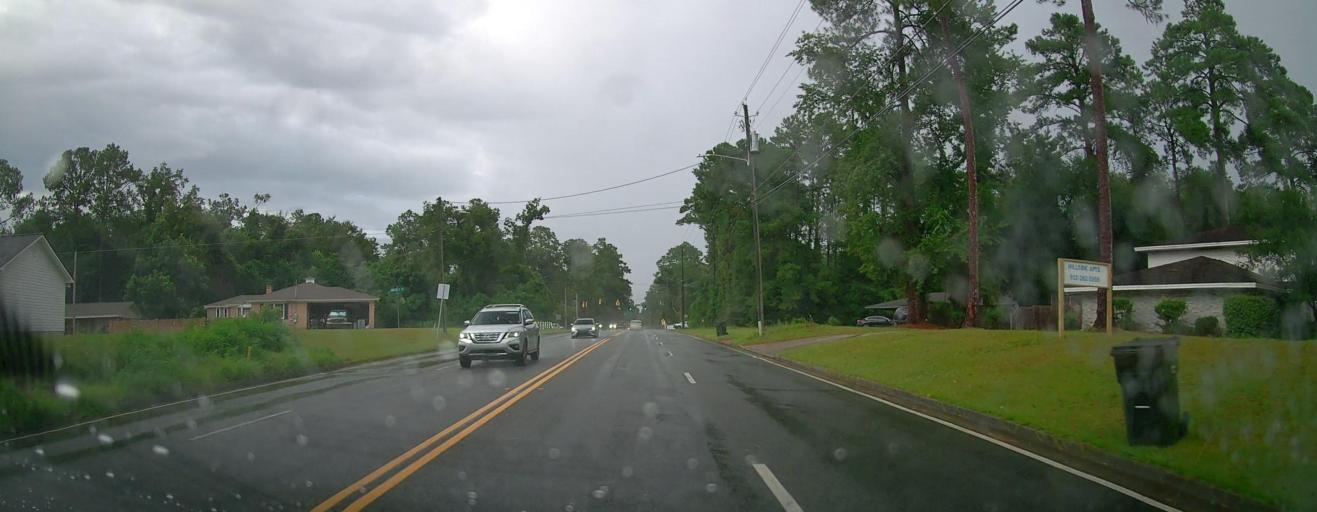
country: US
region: Georgia
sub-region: Ware County
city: Waycross
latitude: 31.2125
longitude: -82.3306
